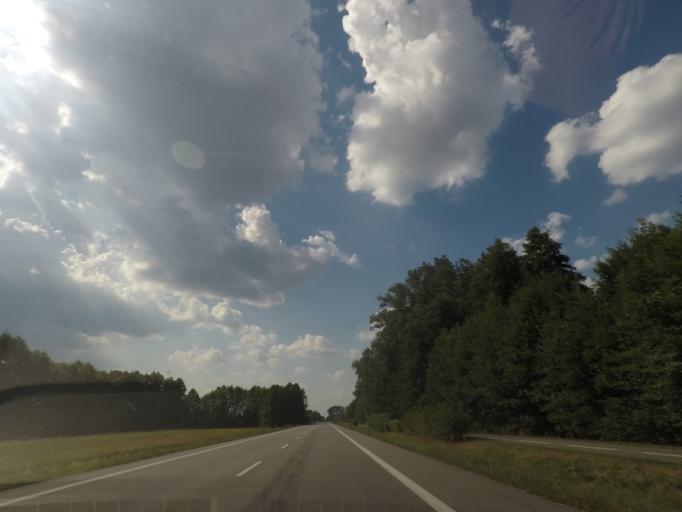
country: CZ
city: Tyniste nad Orlici
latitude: 50.1607
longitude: 16.0581
